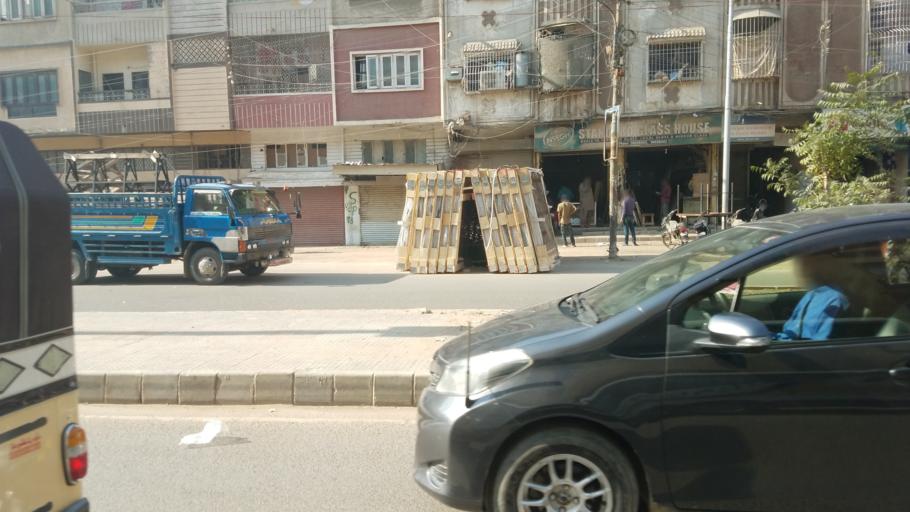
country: PK
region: Sindh
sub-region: Karachi District
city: Karachi
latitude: 24.9166
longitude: 67.0554
